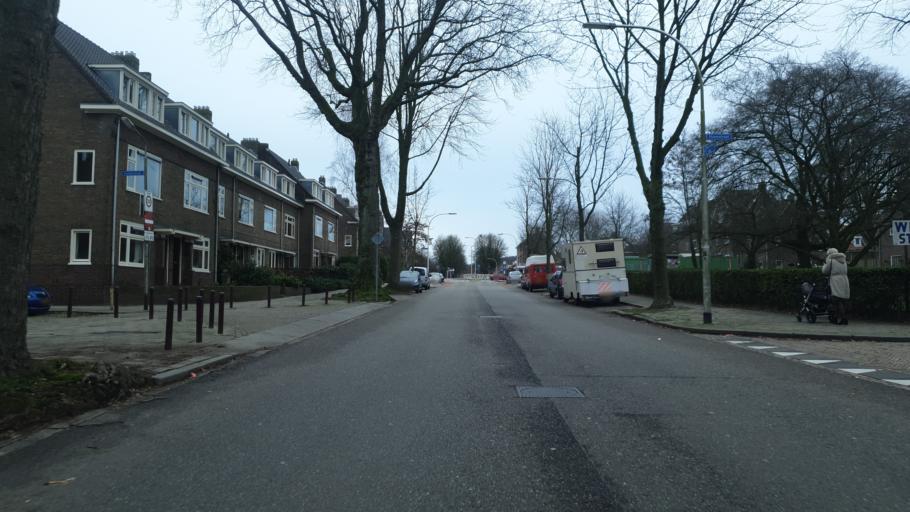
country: NL
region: Gelderland
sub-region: Gemeente Nijmegen
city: Nijmegen
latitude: 51.8340
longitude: 5.8837
